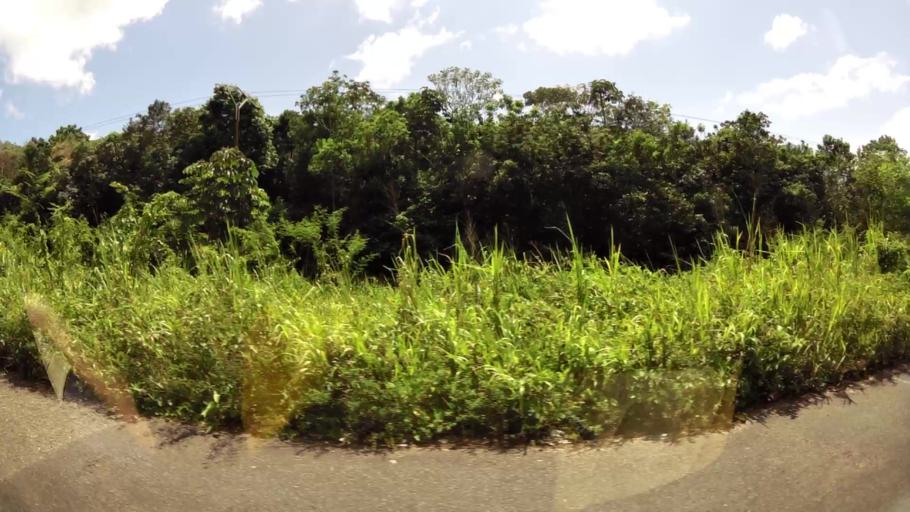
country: GF
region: Guyane
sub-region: Guyane
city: Matoury
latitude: 4.8665
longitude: -52.3346
